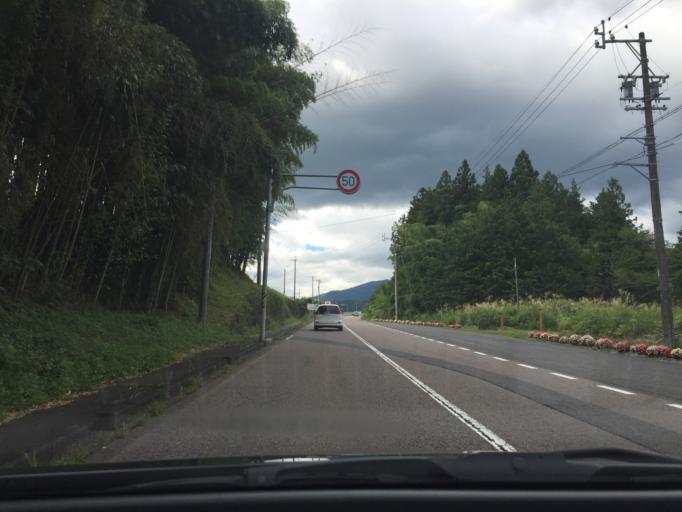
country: JP
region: Gifu
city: Nakatsugawa
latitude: 35.7381
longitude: 137.3426
